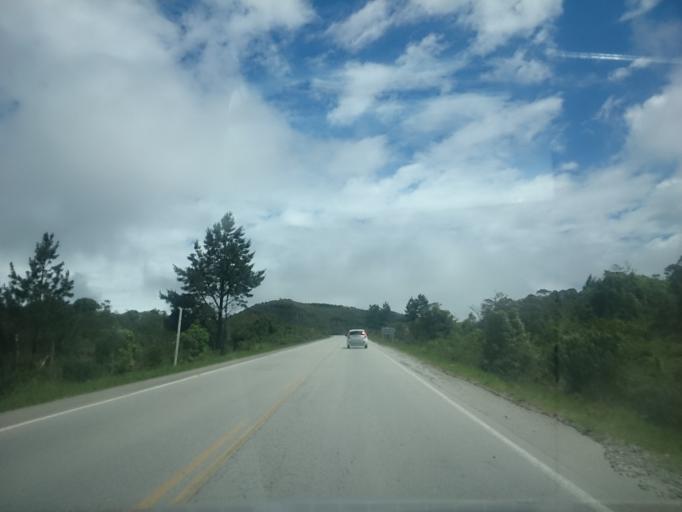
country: BR
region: Santa Catarina
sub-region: Anitapolis
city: Anitapolis
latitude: -27.6845
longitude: -49.1169
